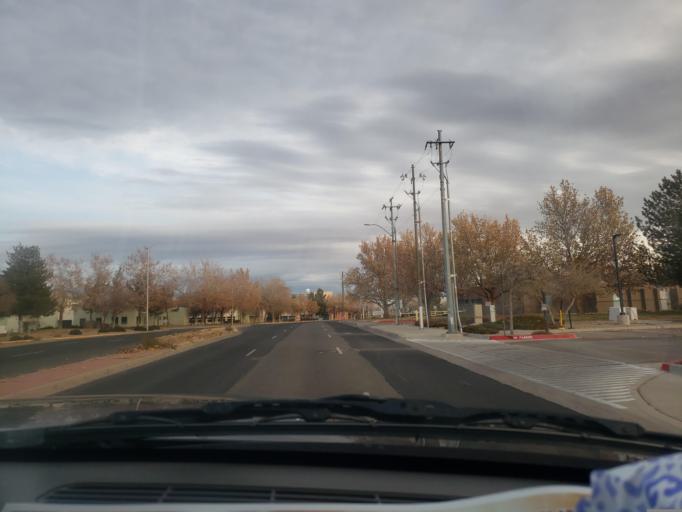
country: US
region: New Mexico
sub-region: Bernalillo County
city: Albuquerque
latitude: 35.0703
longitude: -106.6309
